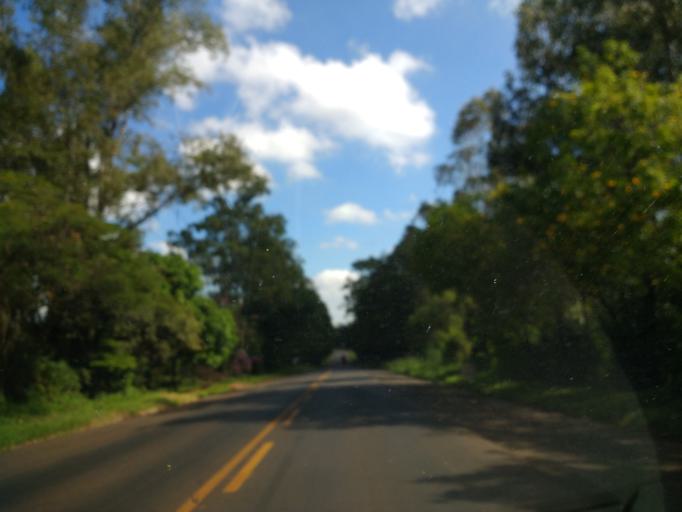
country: BR
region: Parana
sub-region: Umuarama
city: Umuarama
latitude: -23.8265
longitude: -53.3435
